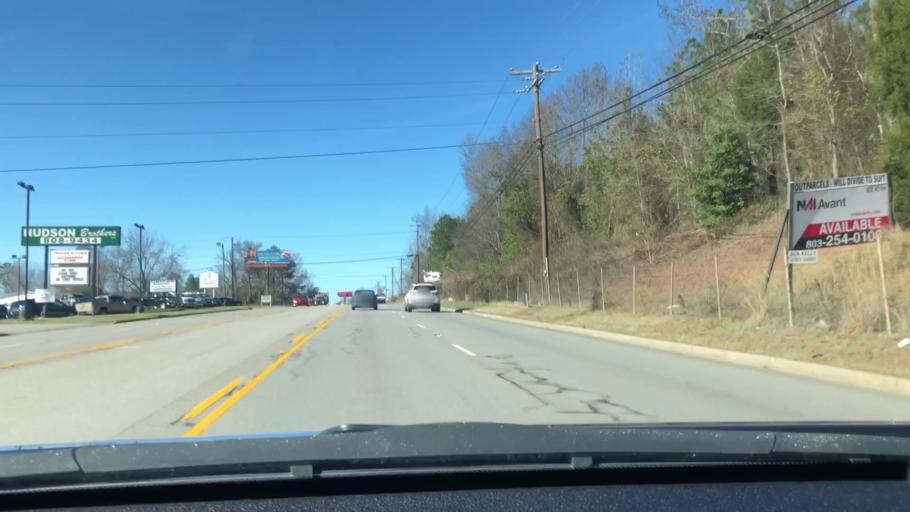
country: US
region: South Carolina
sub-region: Lexington County
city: Oak Grove
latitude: 34.0129
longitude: -81.1760
